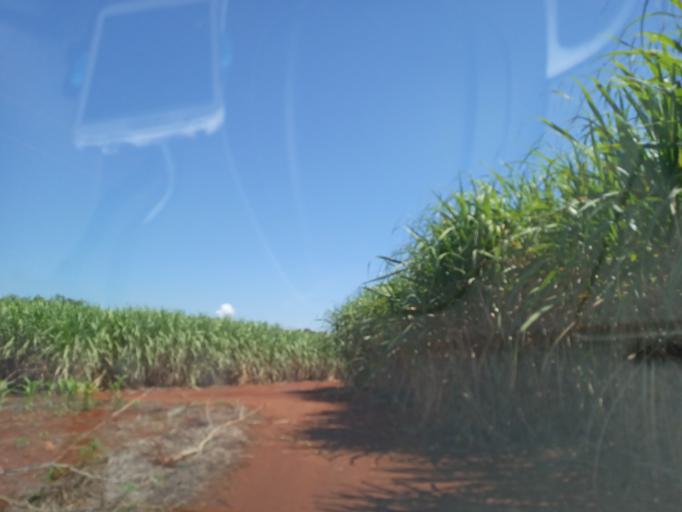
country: BR
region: Goias
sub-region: Itumbiara
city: Itumbiara
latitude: -18.4444
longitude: -49.1404
